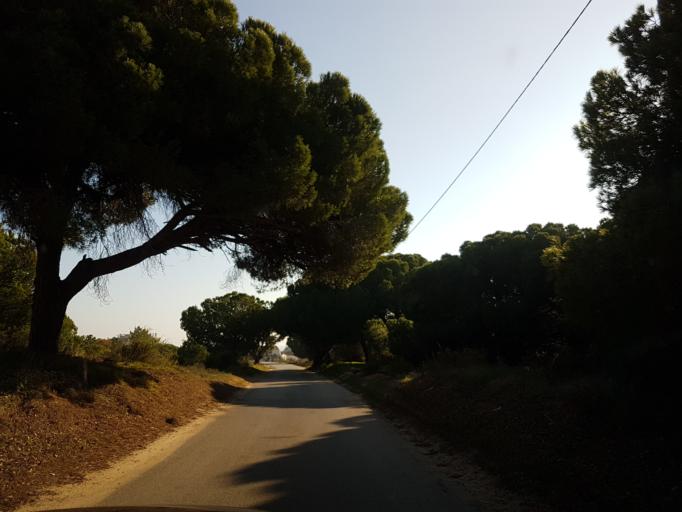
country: PT
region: Faro
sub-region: Albufeira
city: Ferreiras
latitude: 37.0977
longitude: -8.2046
